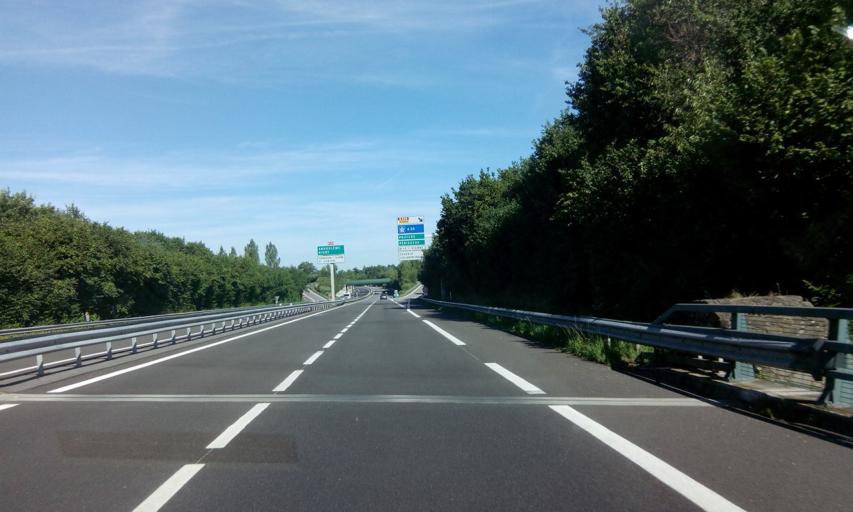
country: FR
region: Limousin
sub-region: Departement de la Haute-Vienne
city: Aixe-sur-Vienne
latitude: 45.8517
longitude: 1.1604
